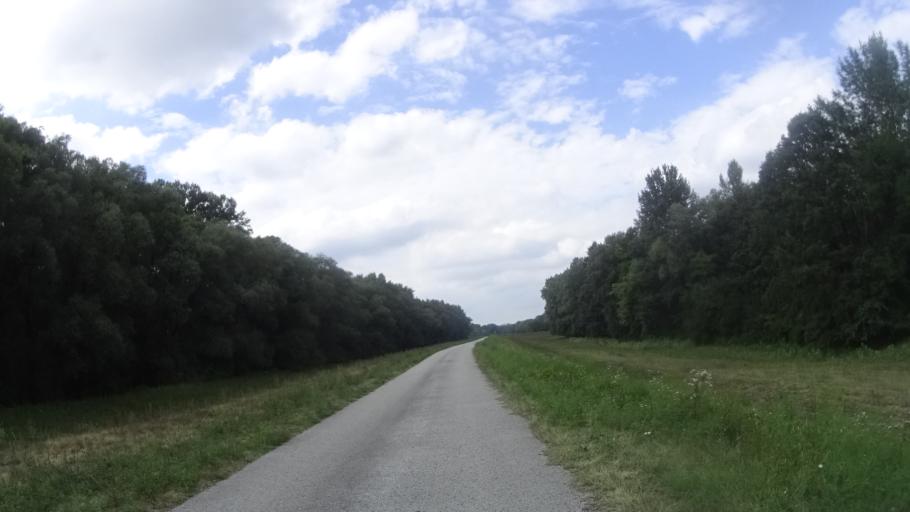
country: SK
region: Trnavsky
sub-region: Okres Dunajska Streda
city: Velky Meder
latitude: 47.7769
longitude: 17.7070
